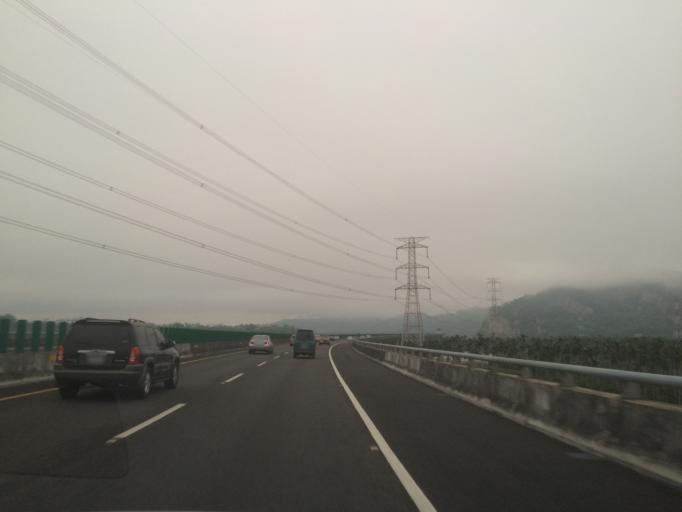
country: TW
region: Taiwan
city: Zhongxing New Village
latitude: 23.9856
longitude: 120.7583
